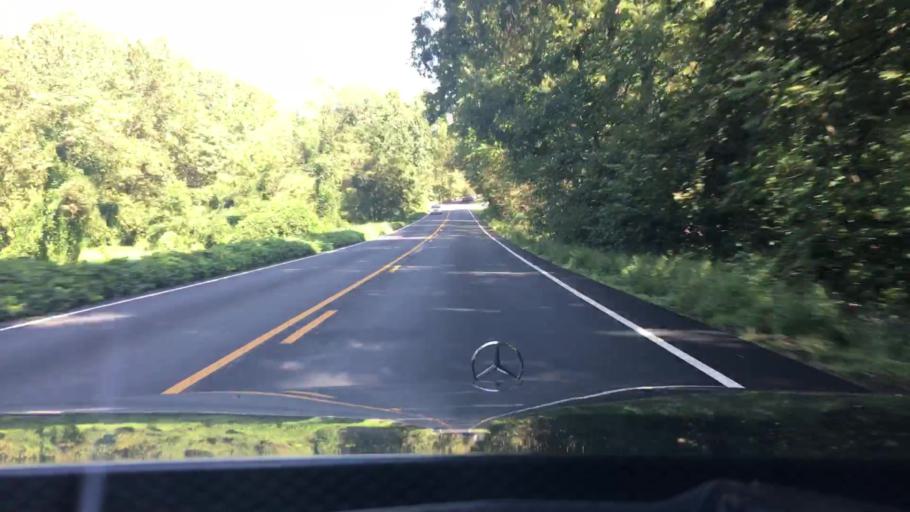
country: US
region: Virginia
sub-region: Nelson County
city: Nellysford
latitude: 37.8999
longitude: -78.8321
